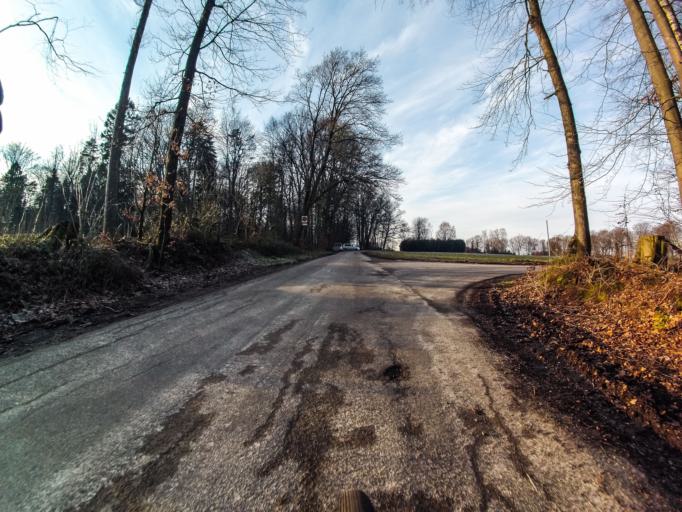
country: DE
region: North Rhine-Westphalia
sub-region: Regierungsbezirk Munster
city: Mettingen
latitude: 52.2906
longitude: 7.7943
